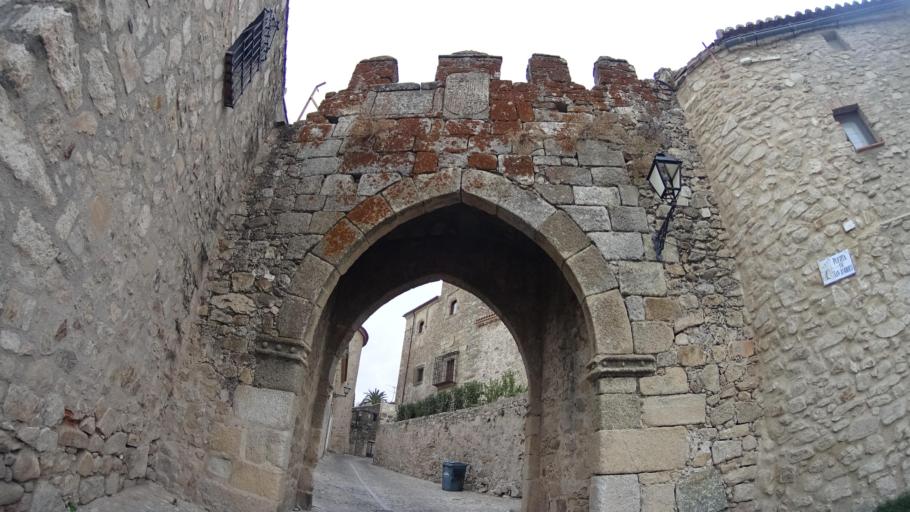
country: ES
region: Extremadura
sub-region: Provincia de Caceres
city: Trujillo
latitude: 39.4594
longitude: -5.8845
